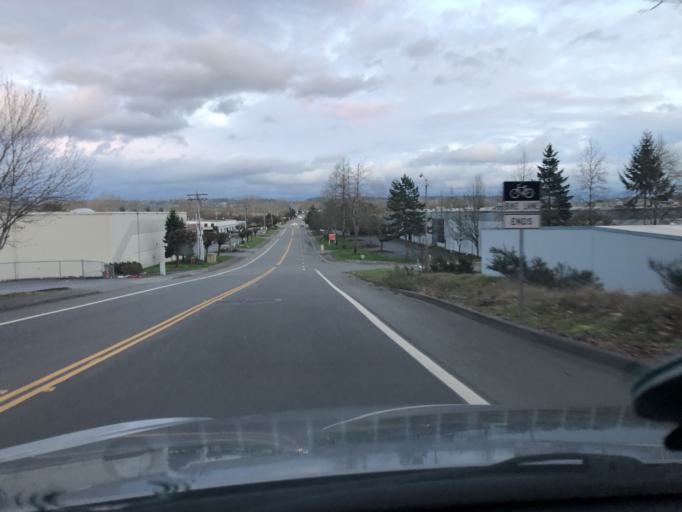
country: US
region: Washington
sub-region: King County
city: Lakeland North
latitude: 47.3225
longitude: -122.2548
